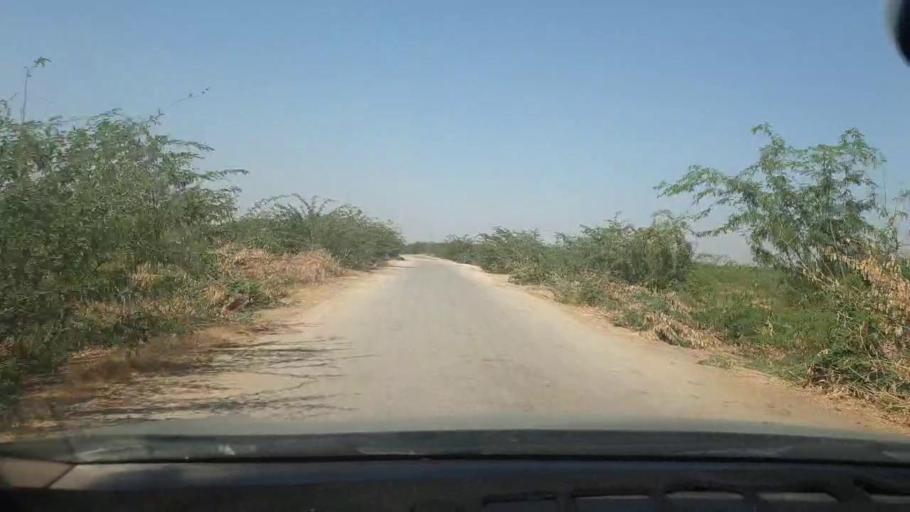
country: PK
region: Sindh
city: Malir Cantonment
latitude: 25.1597
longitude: 67.1636
